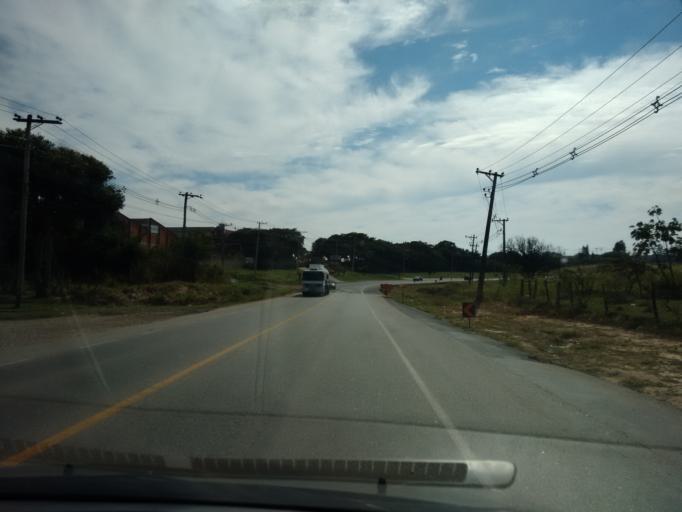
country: BR
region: Sao Paulo
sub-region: Itu
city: Itu
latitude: -23.3015
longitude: -47.3036
